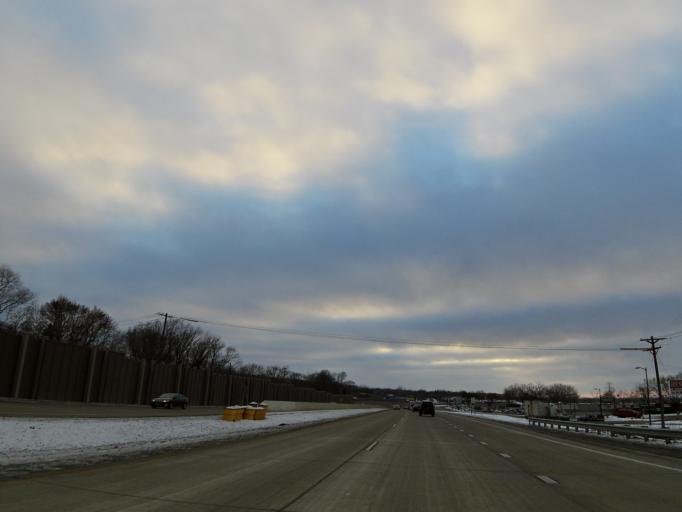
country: US
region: Minnesota
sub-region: Dakota County
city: Burnsville
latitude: 44.7742
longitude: -93.2953
